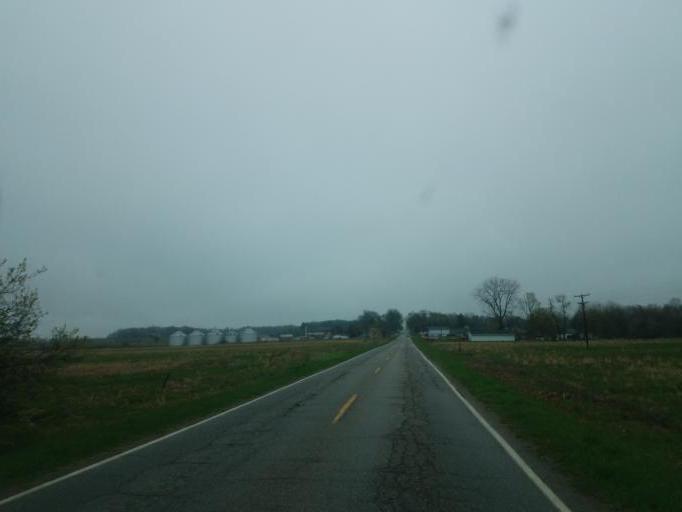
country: US
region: Michigan
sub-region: Isabella County
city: Lake Isabella
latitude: 43.5252
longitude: -84.9110
